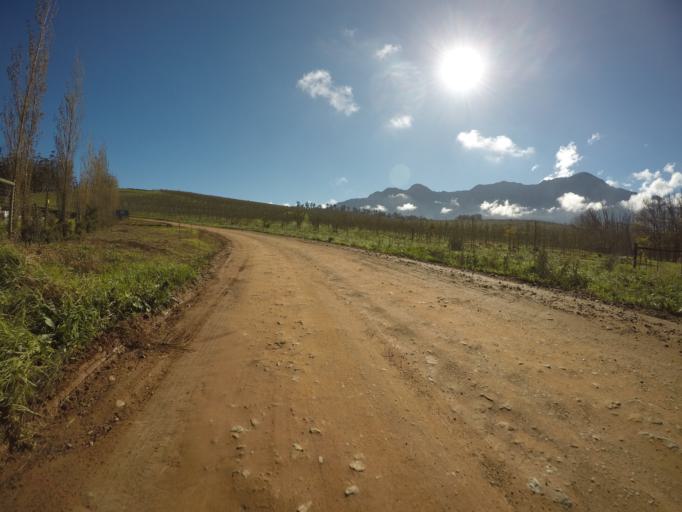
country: ZA
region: Western Cape
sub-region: Overberg District Municipality
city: Caledon
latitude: -34.0953
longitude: 19.6962
